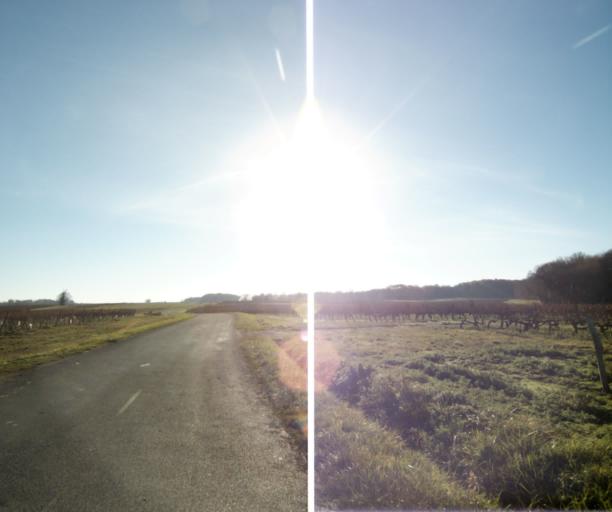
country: FR
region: Poitou-Charentes
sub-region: Departement de la Charente-Maritime
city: Cherac
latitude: 45.7359
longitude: -0.4335
